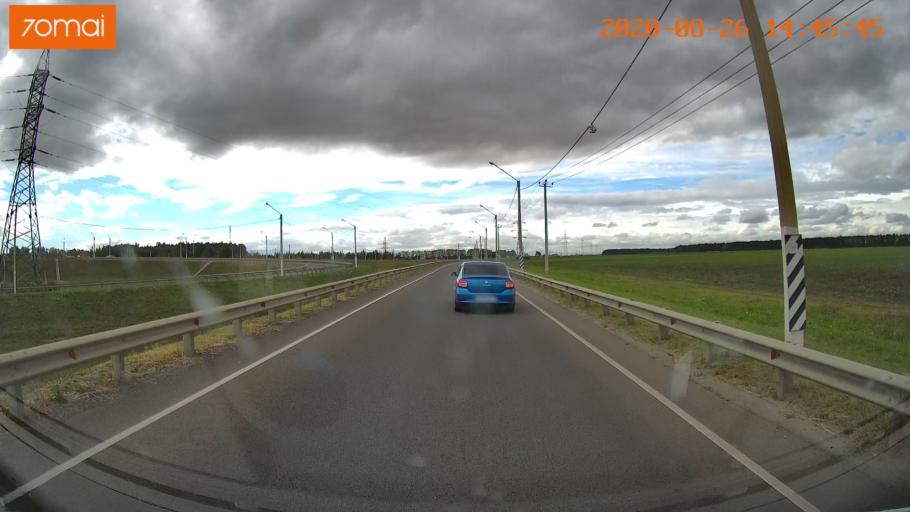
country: RU
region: Rjazan
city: Mikhaylov
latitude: 54.2476
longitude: 39.0554
